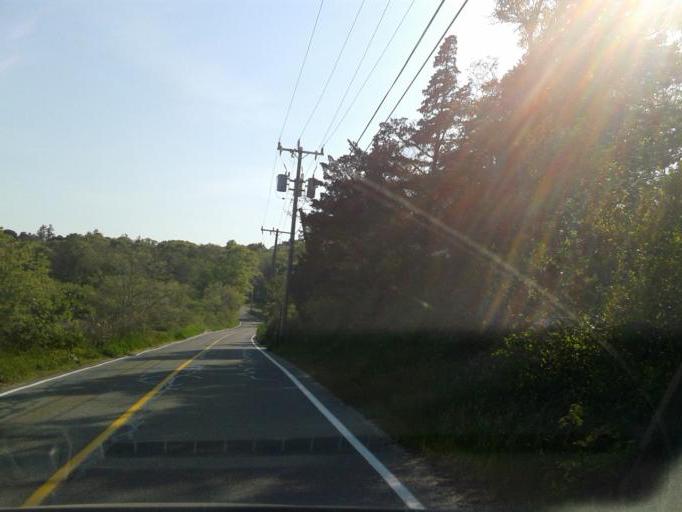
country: US
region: Massachusetts
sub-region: Barnstable County
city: Falmouth
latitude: 41.5342
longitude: -70.6441
